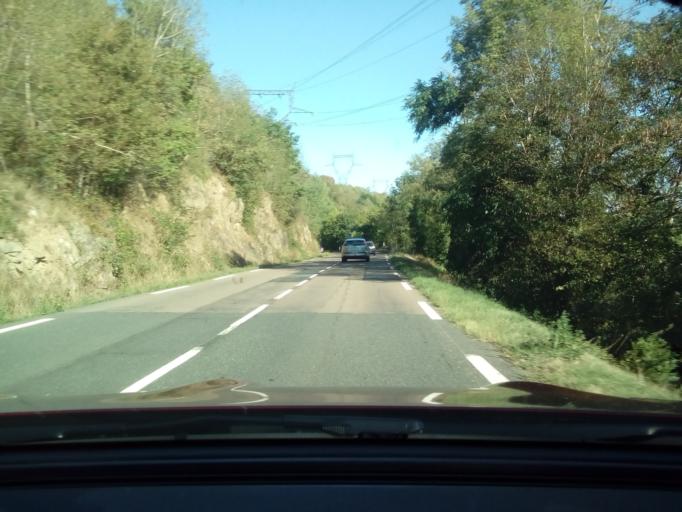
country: FR
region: Rhone-Alpes
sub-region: Departement du Rhone
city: Saint-Verand
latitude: 45.9083
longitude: 4.5176
